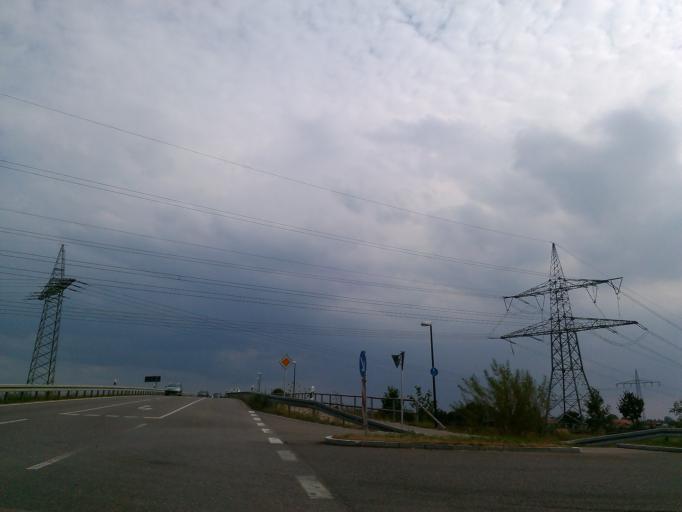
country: DE
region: Bavaria
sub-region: Upper Bavaria
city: Puchheim
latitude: 48.1450
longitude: 11.3513
